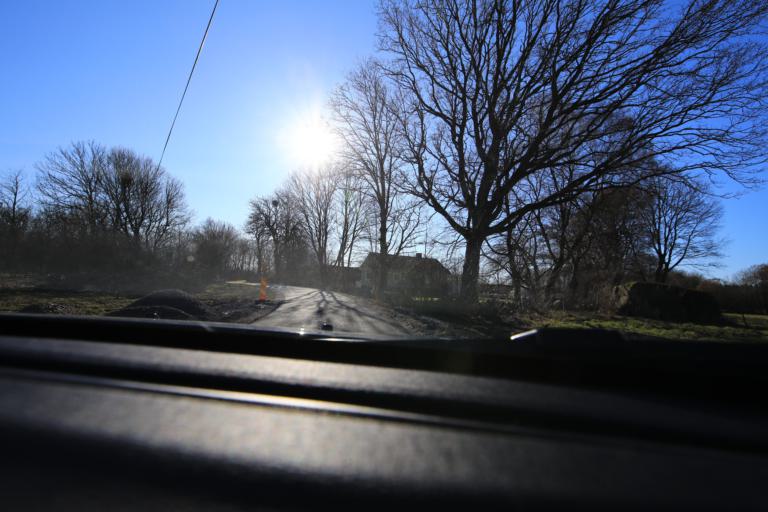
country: SE
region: Halland
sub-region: Varbergs Kommun
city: Tvaaker
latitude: 57.0496
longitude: 12.3769
